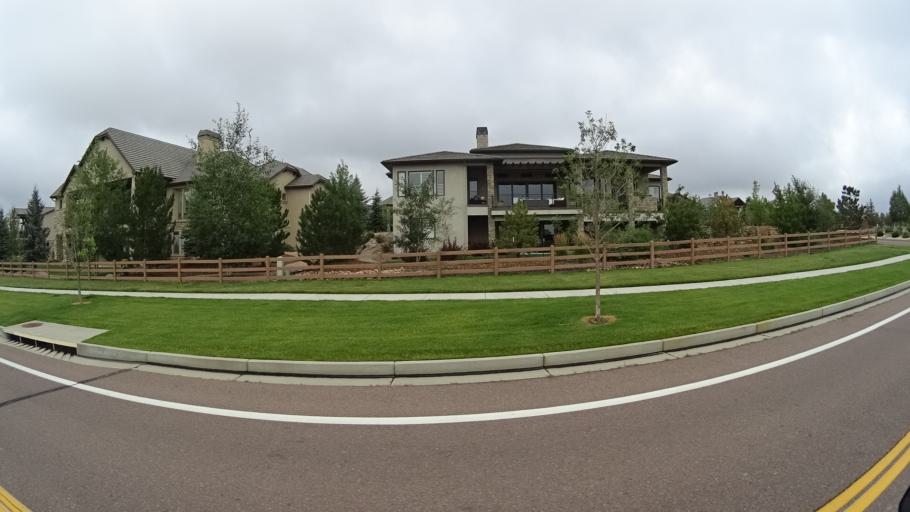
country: US
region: Colorado
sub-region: El Paso County
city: Gleneagle
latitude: 39.0277
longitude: -104.7890
